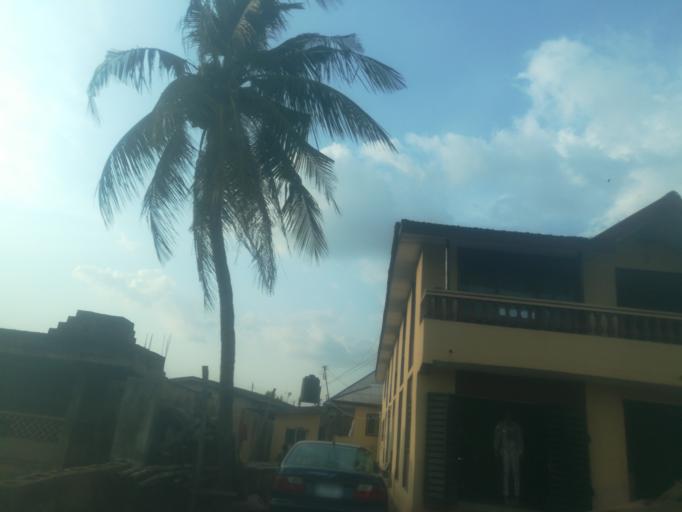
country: NG
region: Ogun
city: Abeokuta
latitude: 7.1605
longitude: 3.3114
